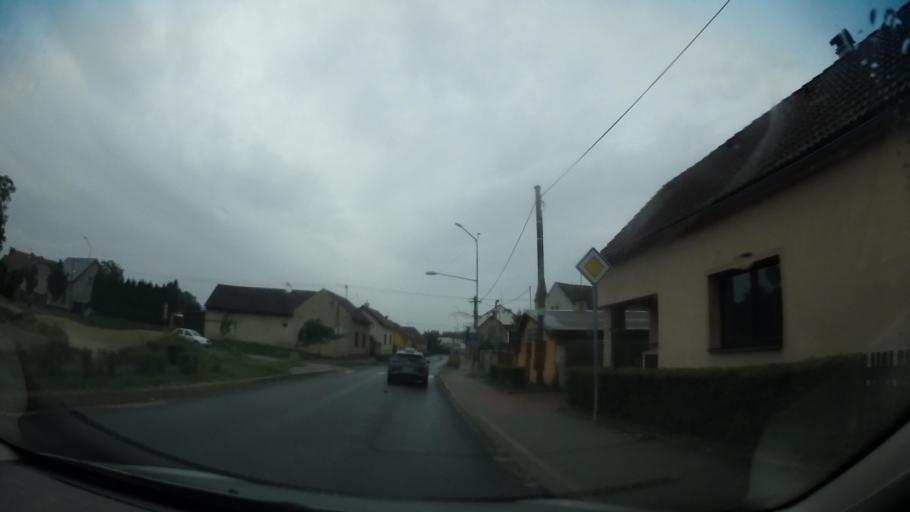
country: CZ
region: Central Bohemia
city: Milovice
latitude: 50.2295
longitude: 14.8852
